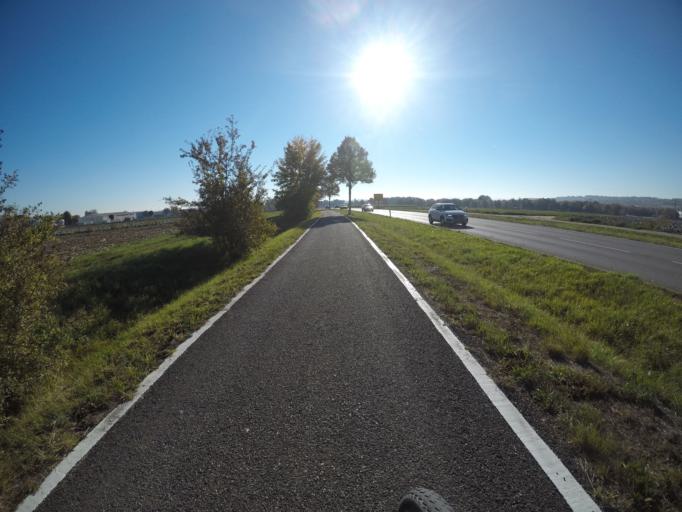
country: DE
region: Baden-Wuerttemberg
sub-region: Regierungsbezirk Stuttgart
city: Leinfelden-Echterdingen
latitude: 48.6795
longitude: 9.1860
